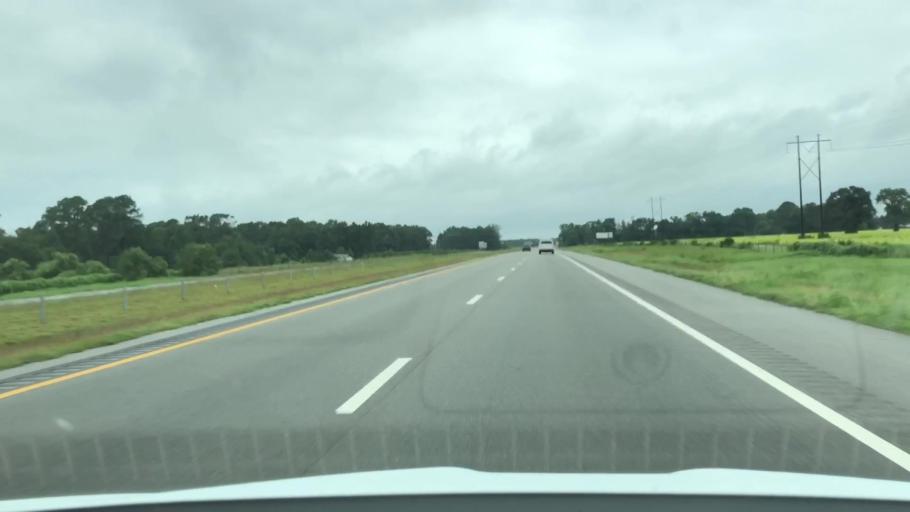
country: US
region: North Carolina
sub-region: Lenoir County
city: La Grange
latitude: 35.3158
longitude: -77.8296
